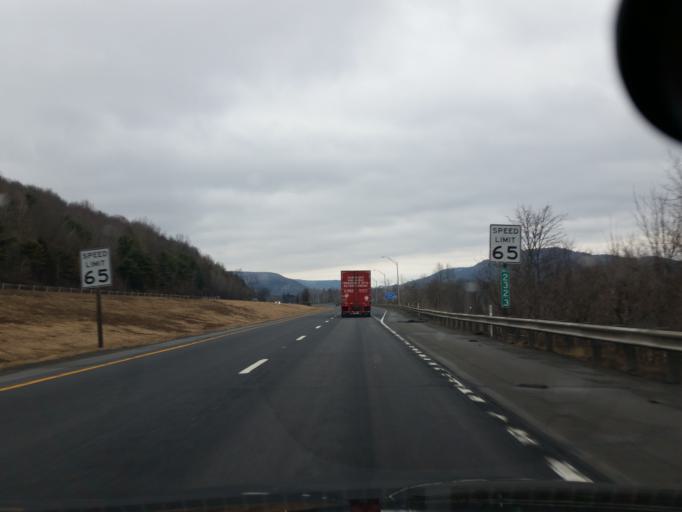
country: US
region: Pennsylvania
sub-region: Susquehanna County
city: Hallstead
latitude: 41.9919
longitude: -75.7507
